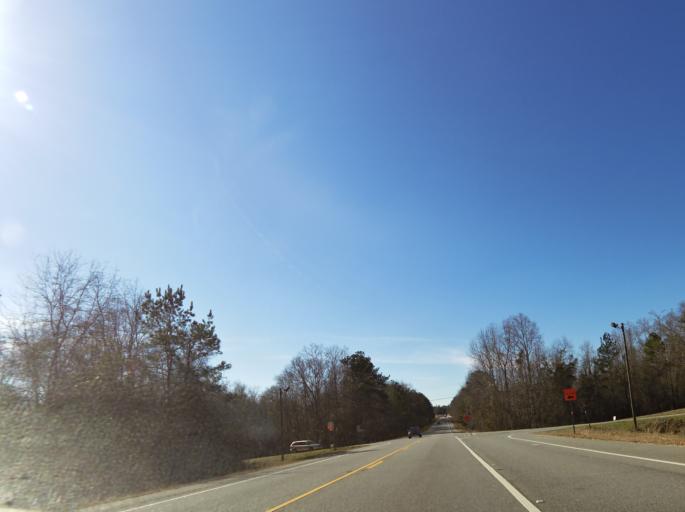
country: US
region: Georgia
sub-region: Bibb County
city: West Point
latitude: 32.7997
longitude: -83.7940
